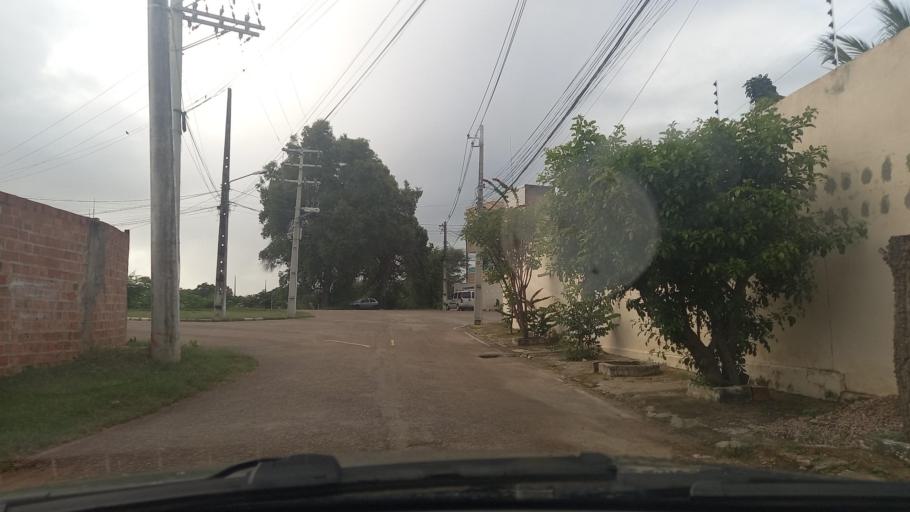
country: BR
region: Bahia
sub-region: Paulo Afonso
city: Paulo Afonso
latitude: -9.3946
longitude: -38.2149
